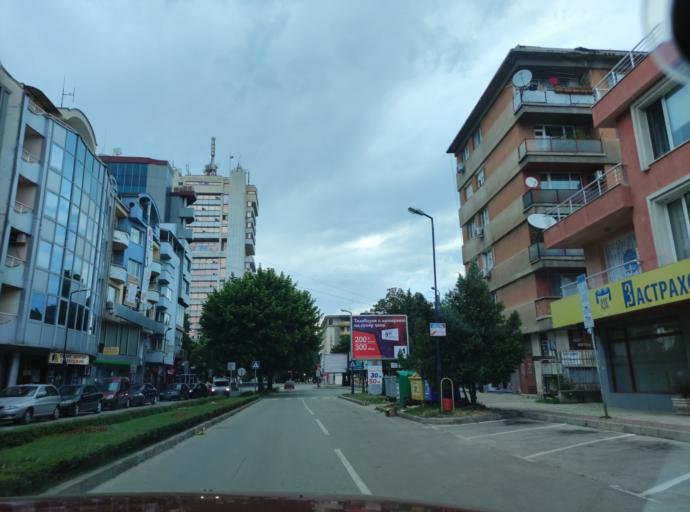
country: BG
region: Pazardzhik
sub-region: Obshtina Pazardzhik
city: Pazardzhik
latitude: 42.1880
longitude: 24.3335
